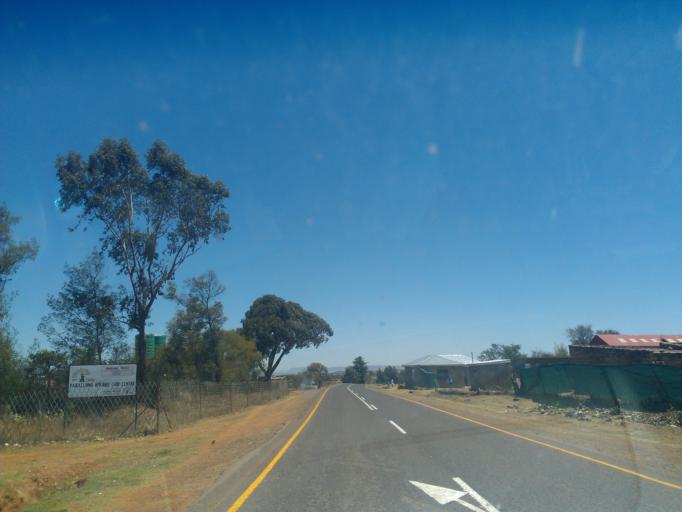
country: LS
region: Berea
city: Teyateyaneng
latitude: -29.2580
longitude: 27.7243
